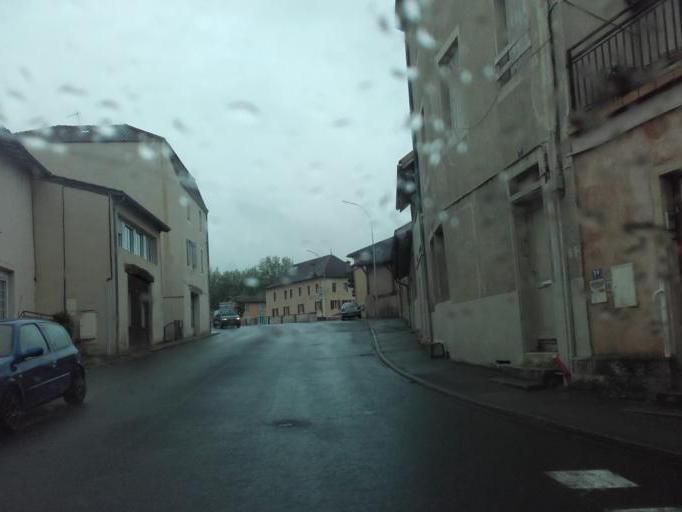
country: FR
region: Bourgogne
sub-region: Departement de Saone-et-Loire
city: Cluny
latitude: 46.4260
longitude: 4.6645
